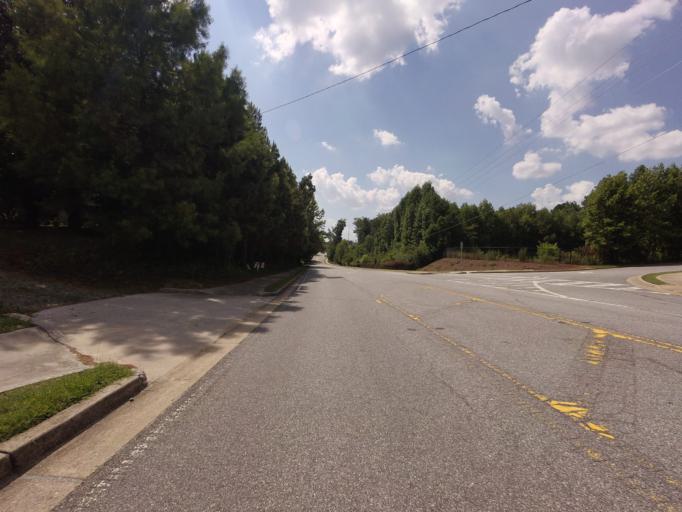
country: US
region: Georgia
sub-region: Fulton County
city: Johns Creek
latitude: 34.0389
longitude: -84.1805
